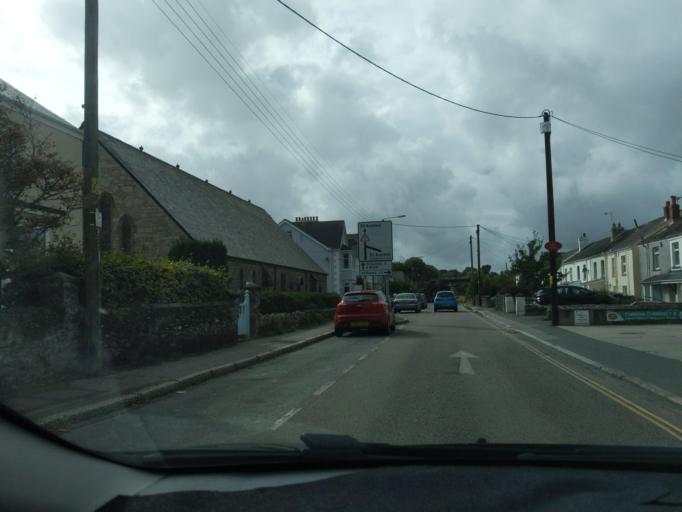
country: GB
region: England
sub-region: Cornwall
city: Par
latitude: 50.3509
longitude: -4.7036
